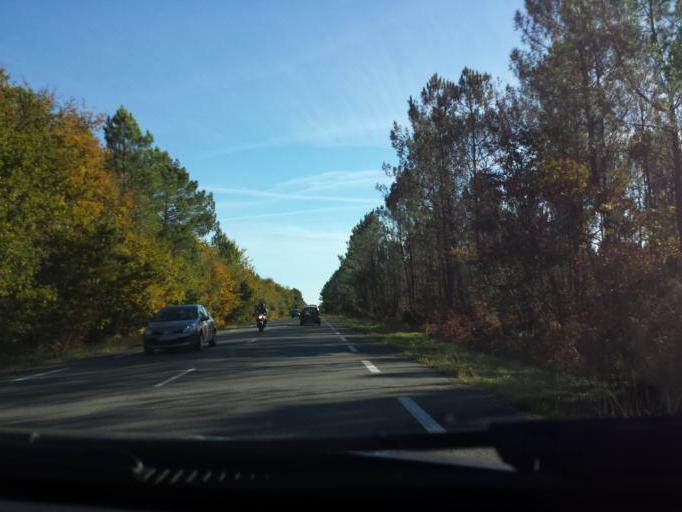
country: FR
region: Aquitaine
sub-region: Departement de la Gironde
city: Lacanau
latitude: 44.9761
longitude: -1.0415
